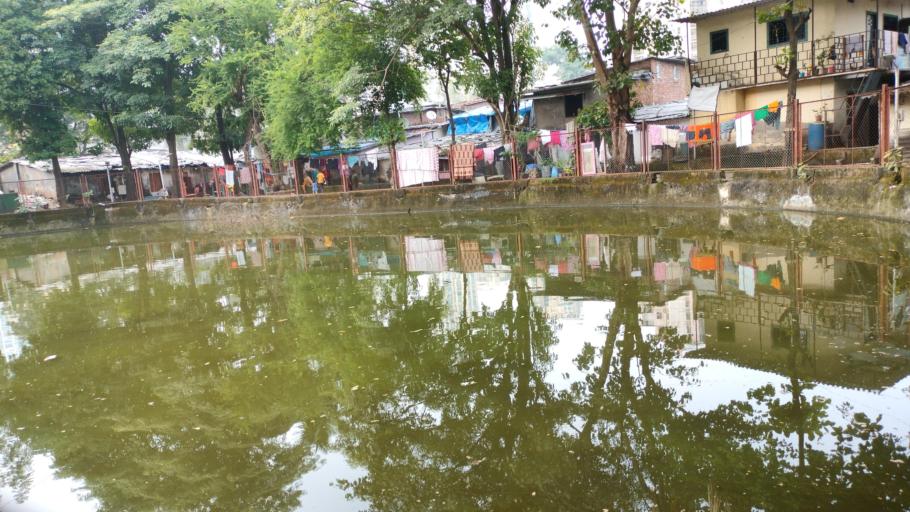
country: IN
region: Maharashtra
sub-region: Thane
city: Thane
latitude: 19.2089
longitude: 72.9765
